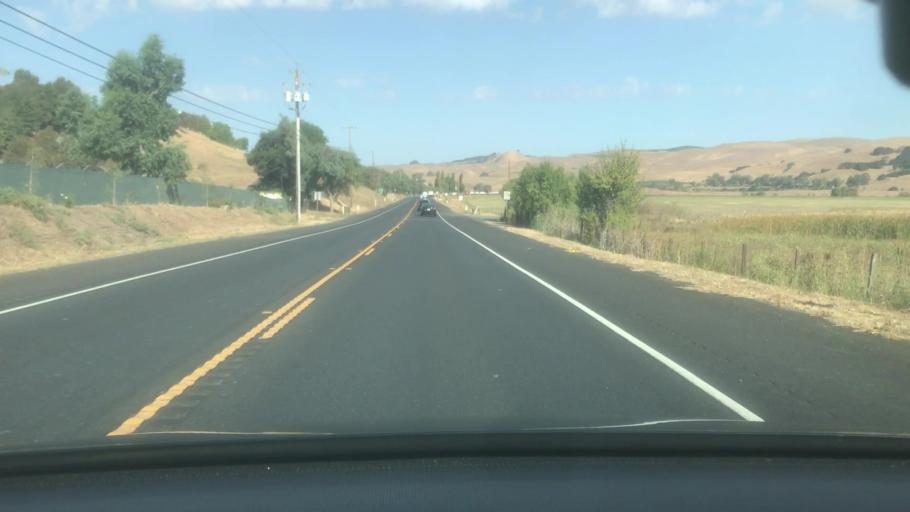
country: US
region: California
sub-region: Marin County
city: Black Point-Green Point
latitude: 38.1627
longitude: -122.4533
